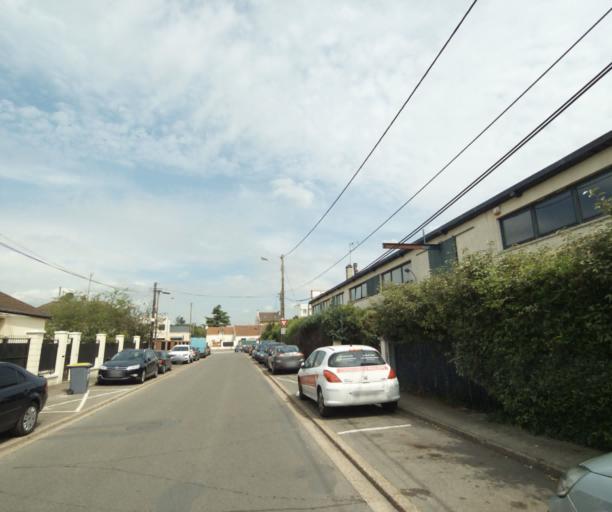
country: FR
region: Ile-de-France
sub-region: Departement des Yvelines
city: Les Mureaux
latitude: 48.9918
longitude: 1.9035
